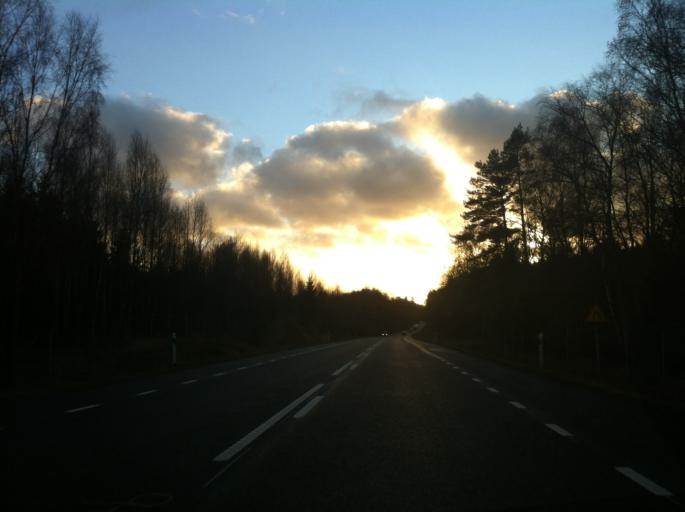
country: SE
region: Skane
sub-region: Hassleholms Kommun
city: Sosdala
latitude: 55.9987
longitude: 13.6390
